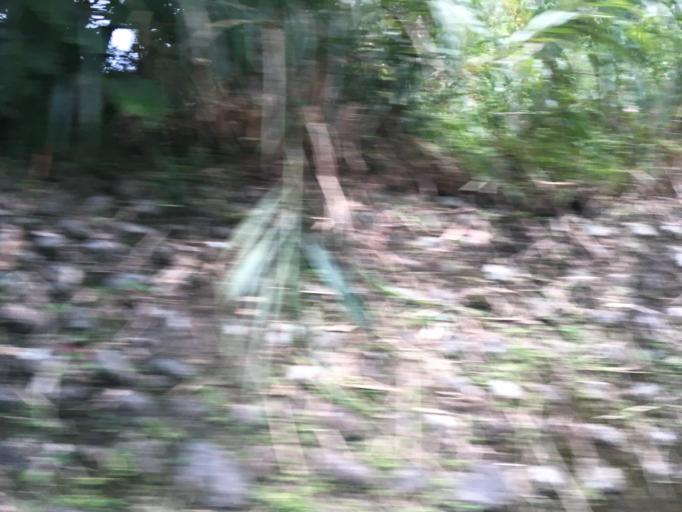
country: TW
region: Taiwan
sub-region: Yilan
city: Yilan
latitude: 24.9308
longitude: 121.6918
